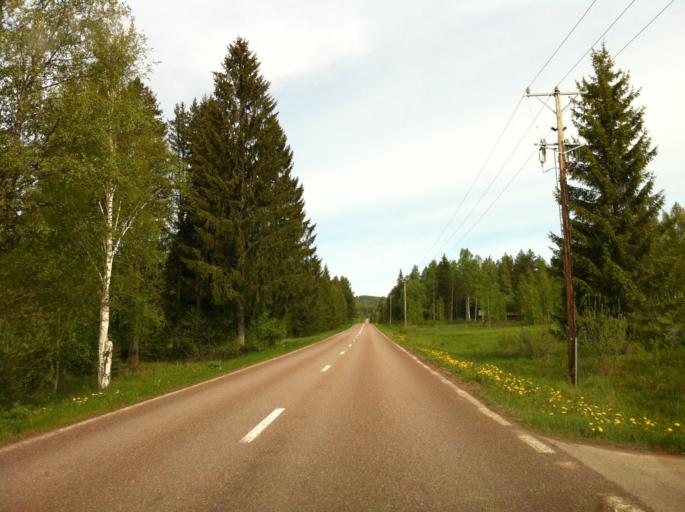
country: SE
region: Dalarna
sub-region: Leksand Municipality
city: Siljansnas
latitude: 60.7774
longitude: 14.7077
